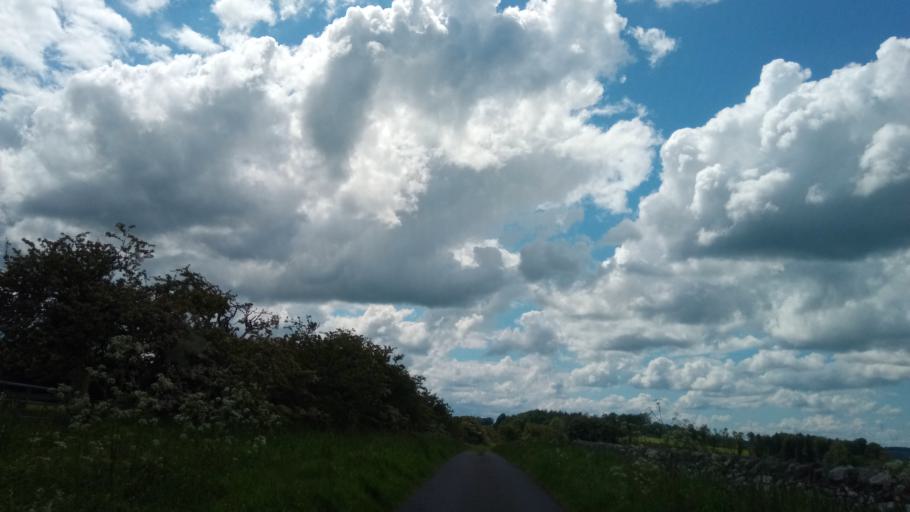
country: GB
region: Scotland
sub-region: The Scottish Borders
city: Coldstream
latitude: 55.5963
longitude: -2.2805
